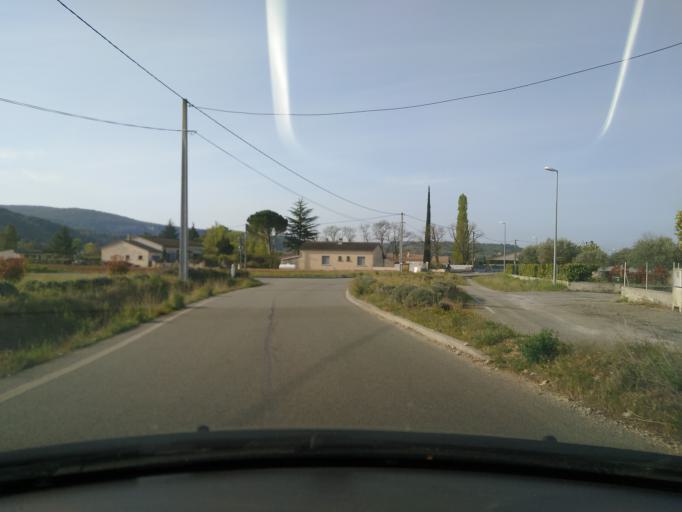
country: FR
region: Rhone-Alpes
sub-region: Departement de l'Ardeche
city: Ruoms
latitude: 44.4187
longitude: 4.4121
